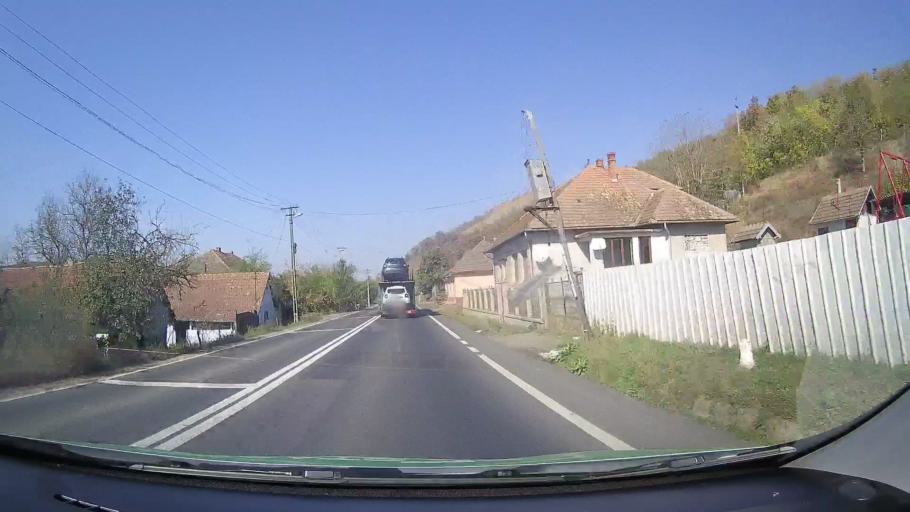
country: RO
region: Arad
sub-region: Comuna Bata
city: Bata
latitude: 46.0512
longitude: 22.0519
